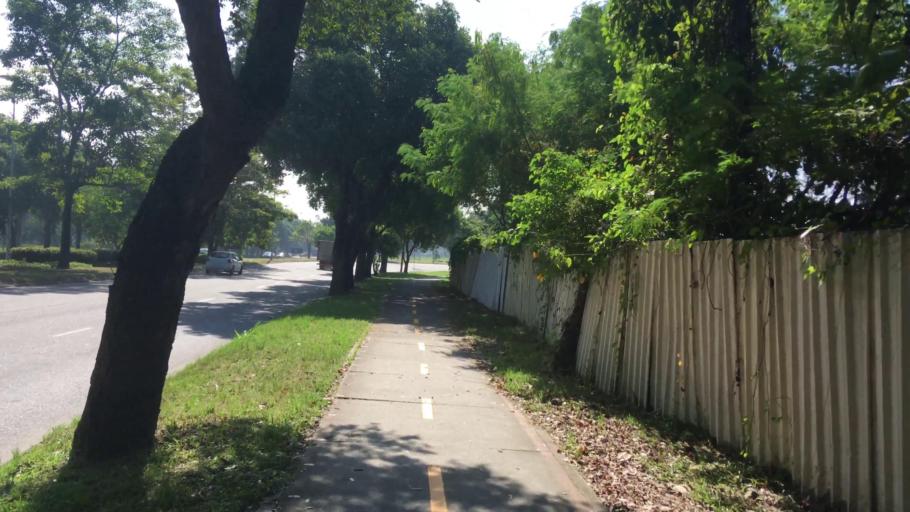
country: BR
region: Rio de Janeiro
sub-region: Rio De Janeiro
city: Rio de Janeiro
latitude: -22.8492
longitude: -43.2354
